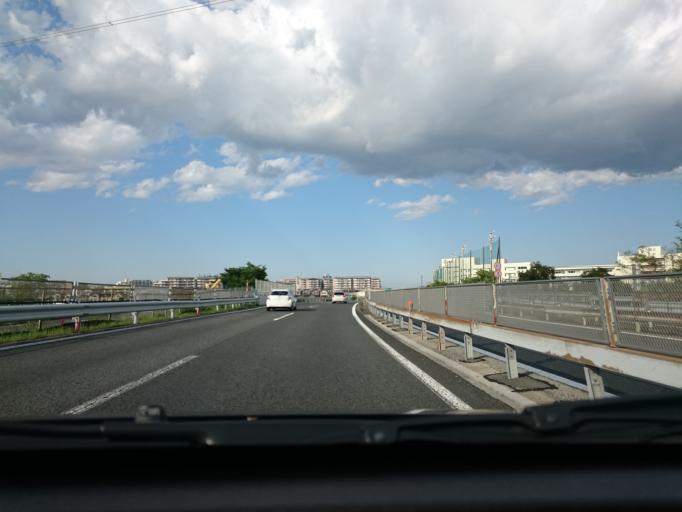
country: JP
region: Kanagawa
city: Isehara
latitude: 35.4042
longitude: 139.3361
